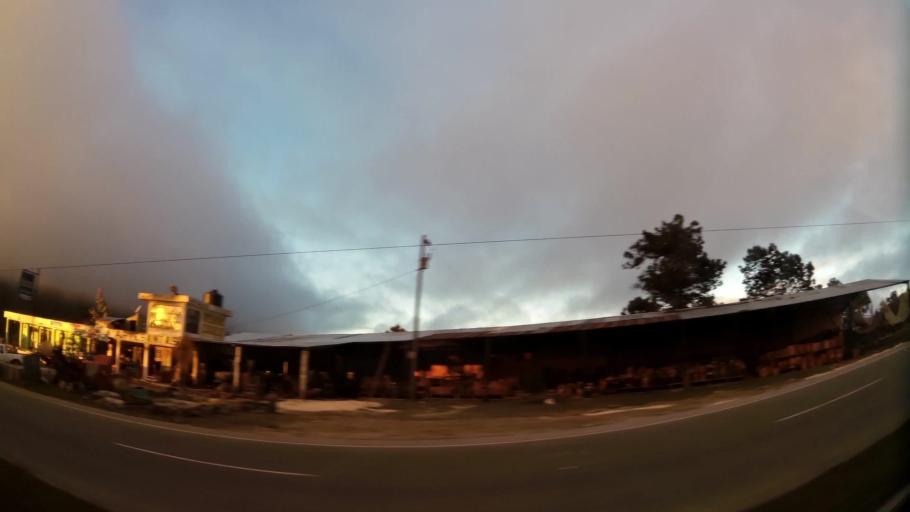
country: GT
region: Solola
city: Concepcion
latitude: 14.8382
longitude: -91.1302
